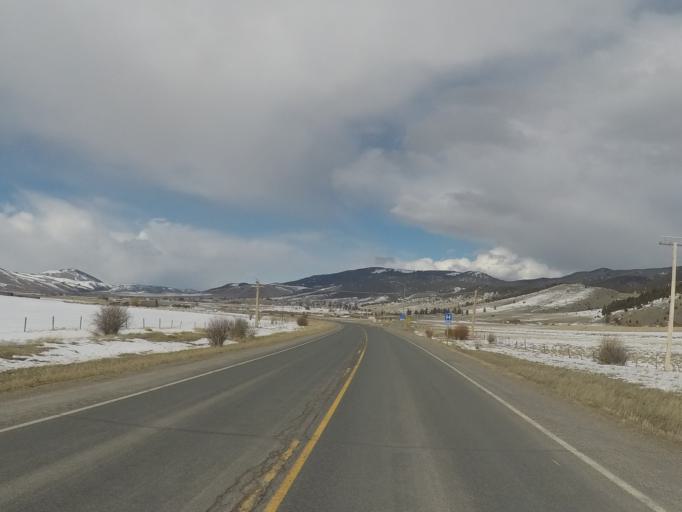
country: US
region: Montana
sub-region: Granite County
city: Philipsburg
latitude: 46.3045
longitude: -113.3089
